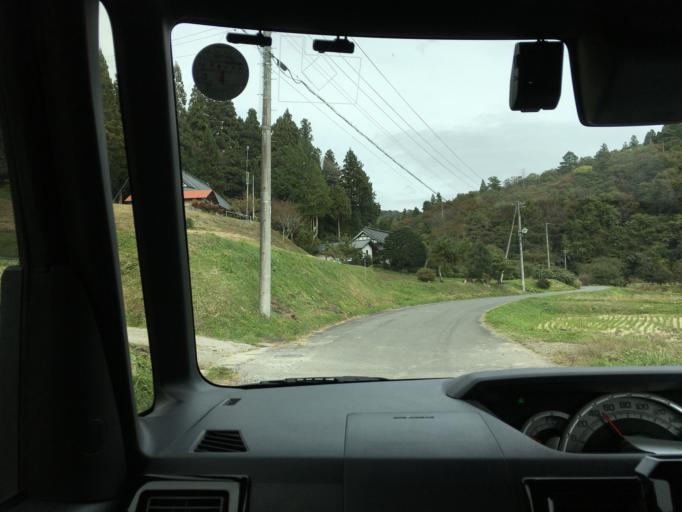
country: JP
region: Iwate
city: Ichinoseki
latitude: 39.0229
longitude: 141.3520
